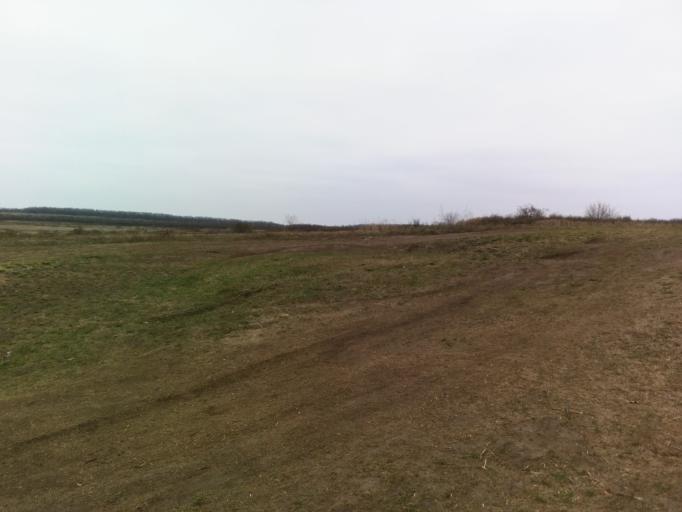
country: RU
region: Voronezj
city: Kalach
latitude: 50.4786
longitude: 41.0731
